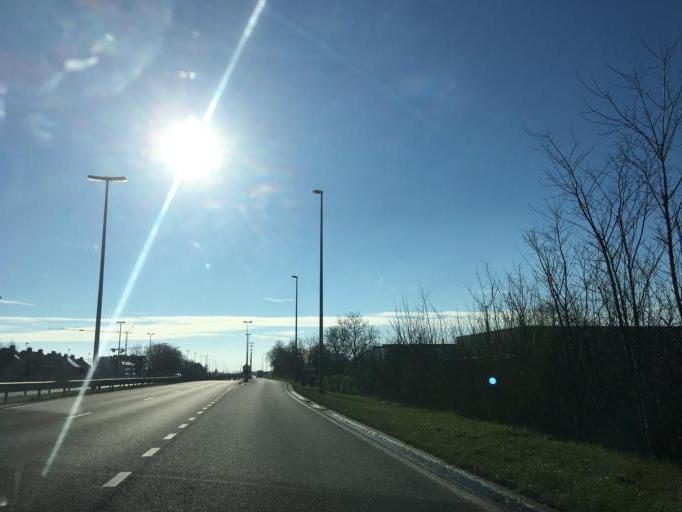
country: BE
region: Flanders
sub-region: Provincie Oost-Vlaanderen
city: Aalter
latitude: 51.0875
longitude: 3.4421
